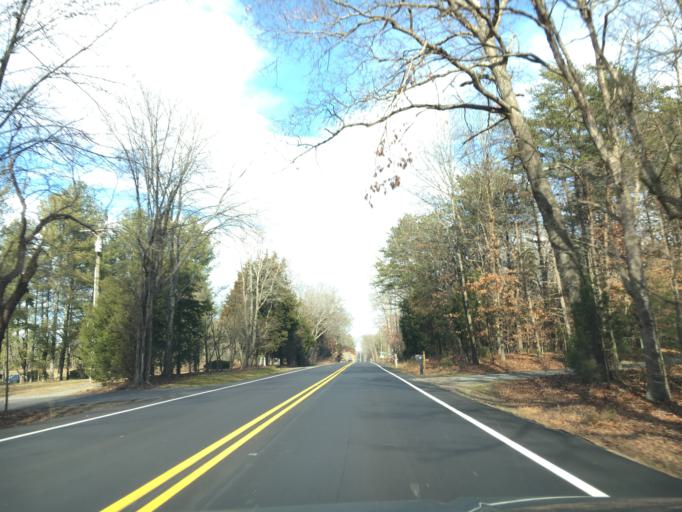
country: US
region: Virginia
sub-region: Orange County
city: Orange
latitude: 38.2938
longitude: -77.9564
